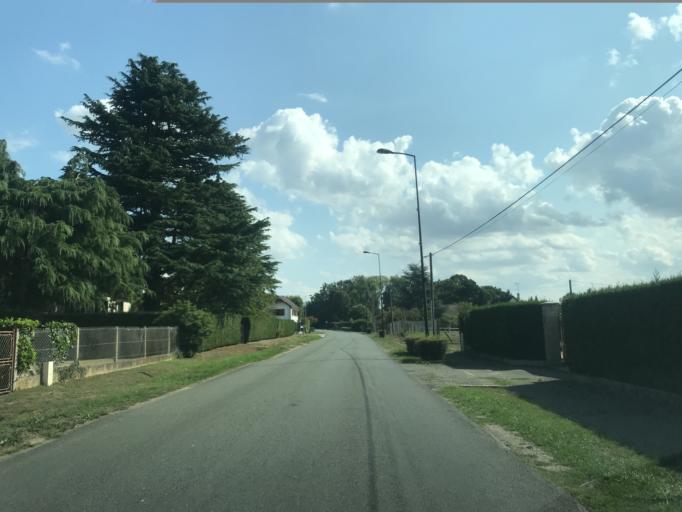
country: FR
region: Haute-Normandie
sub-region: Departement de l'Eure
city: Saint-Aubin-sur-Gaillon
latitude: 49.0877
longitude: 1.2897
